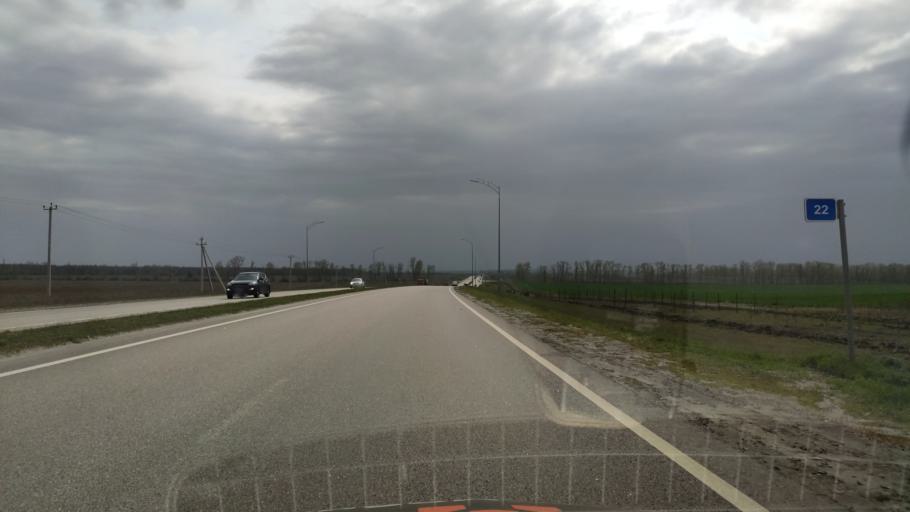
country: RU
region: Belgorod
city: Staryy Oskol
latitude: 51.3960
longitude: 37.8715
